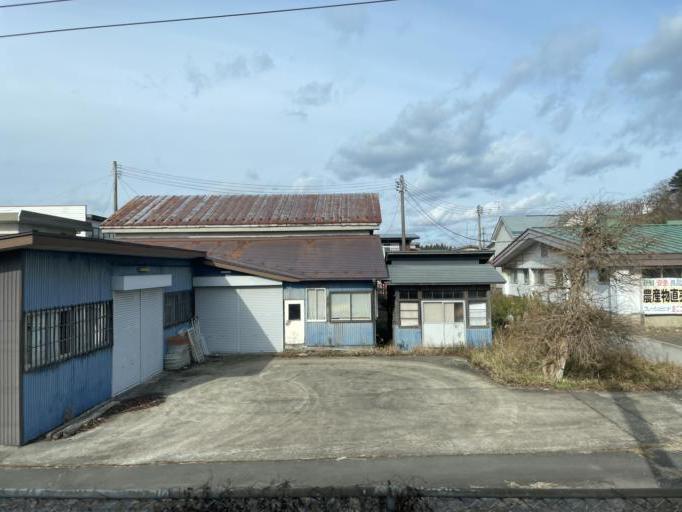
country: JP
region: Akita
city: Akita
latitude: 39.6509
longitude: 140.2171
